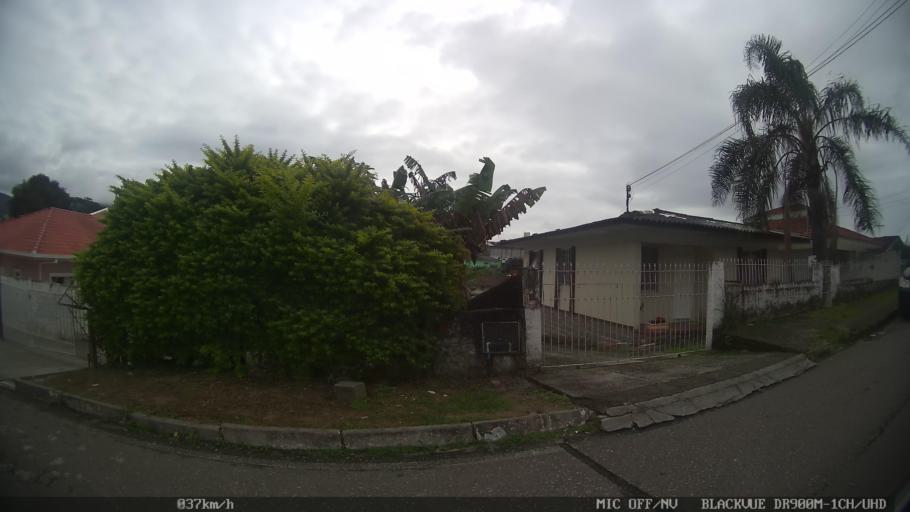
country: BR
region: Santa Catarina
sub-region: Biguacu
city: Biguacu
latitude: -27.5373
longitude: -48.6304
